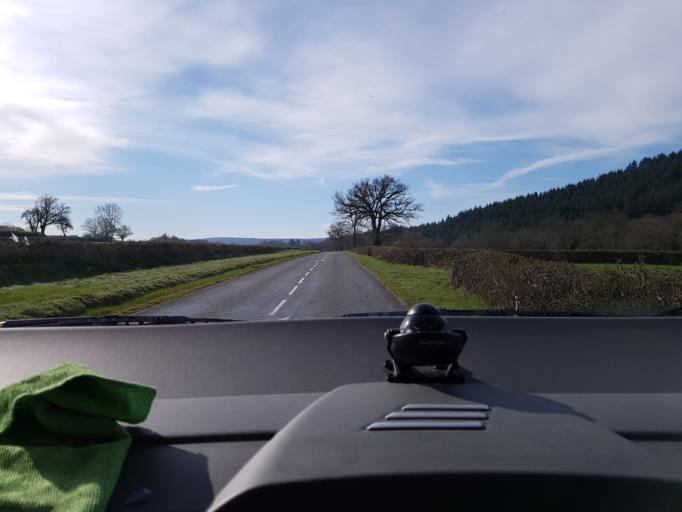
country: FR
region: Bourgogne
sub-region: Departement de Saone-et-Loire
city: Toulon-sur-Arroux
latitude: 46.7228
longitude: 4.1311
